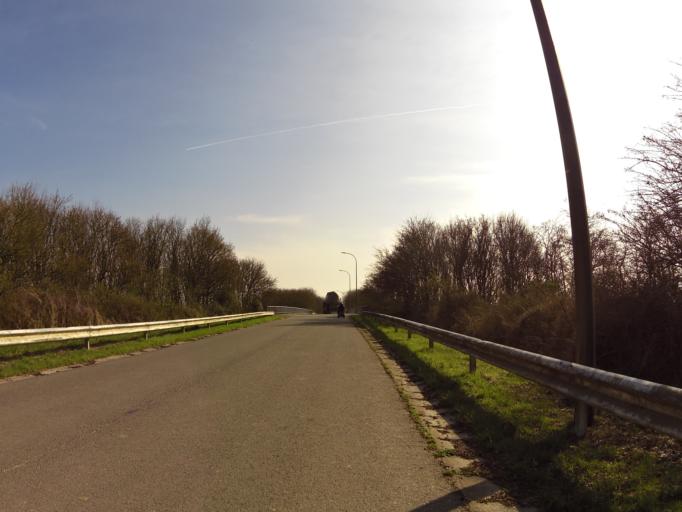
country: BE
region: Flanders
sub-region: Provincie West-Vlaanderen
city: Oudenburg
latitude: 51.1862
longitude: 3.0397
